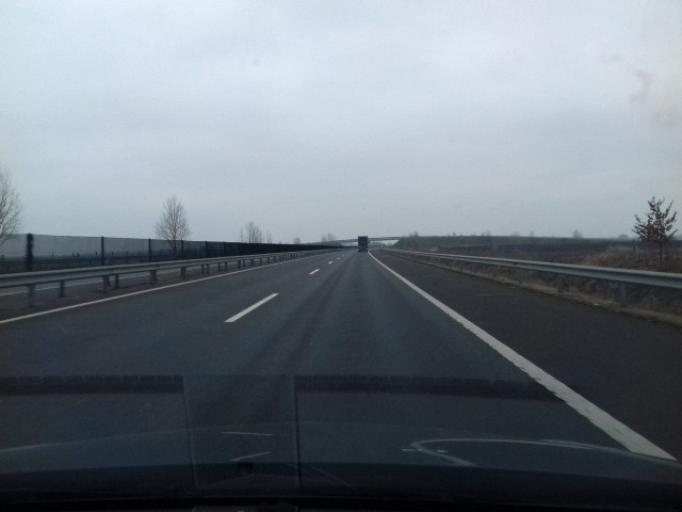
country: HU
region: Hajdu-Bihar
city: Hajdunanas
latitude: 47.8971
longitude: 21.4756
